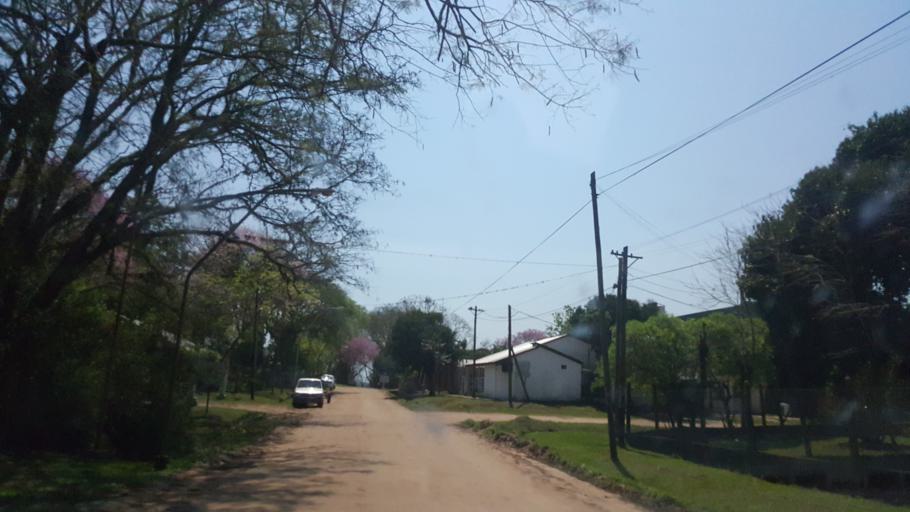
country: AR
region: Corrientes
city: Ita Ibate
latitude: -27.4246
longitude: -57.3331
